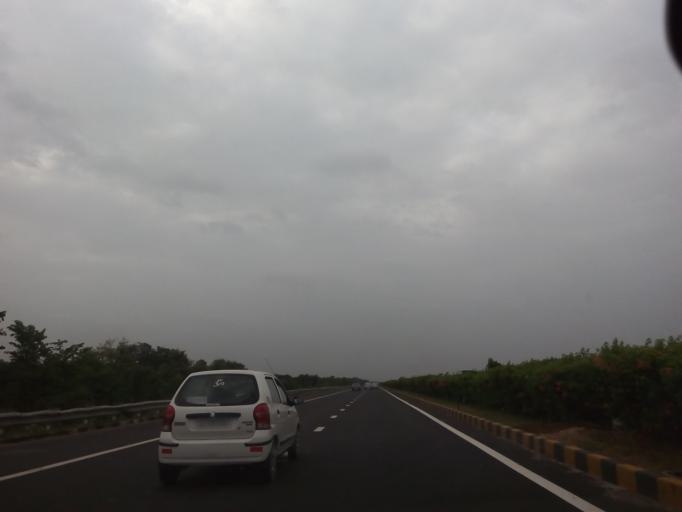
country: IN
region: Gujarat
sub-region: Kheda
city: Chaklasi
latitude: 22.6408
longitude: 72.9375
